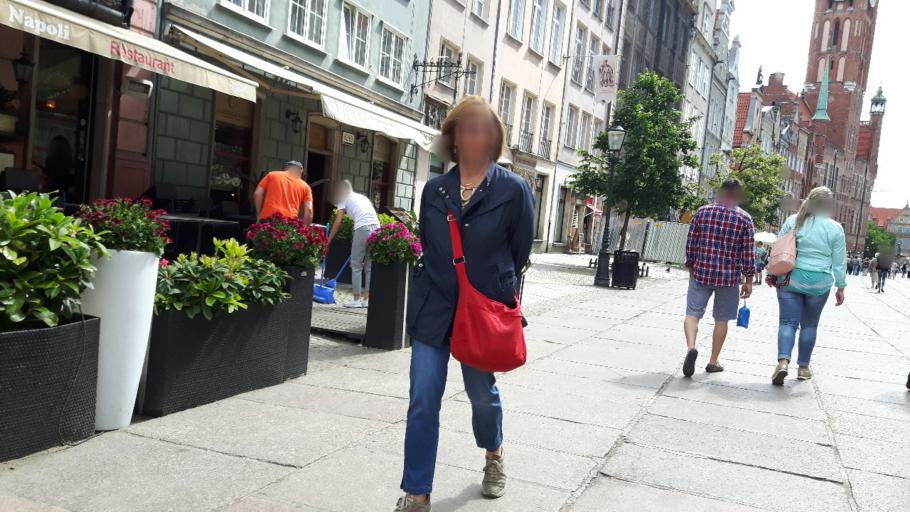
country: PL
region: Pomeranian Voivodeship
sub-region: Gdansk
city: Gdansk
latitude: 54.3490
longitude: 18.6506
